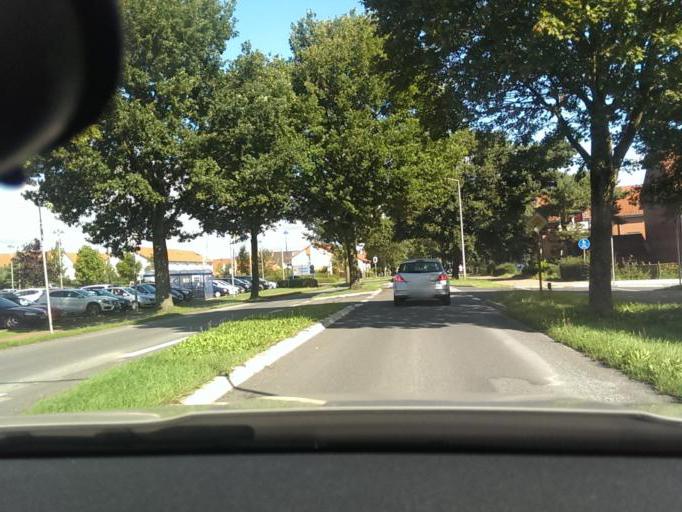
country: DE
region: Lower Saxony
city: Isernhagen Farster Bauerschaft
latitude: 52.4846
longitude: 9.8586
